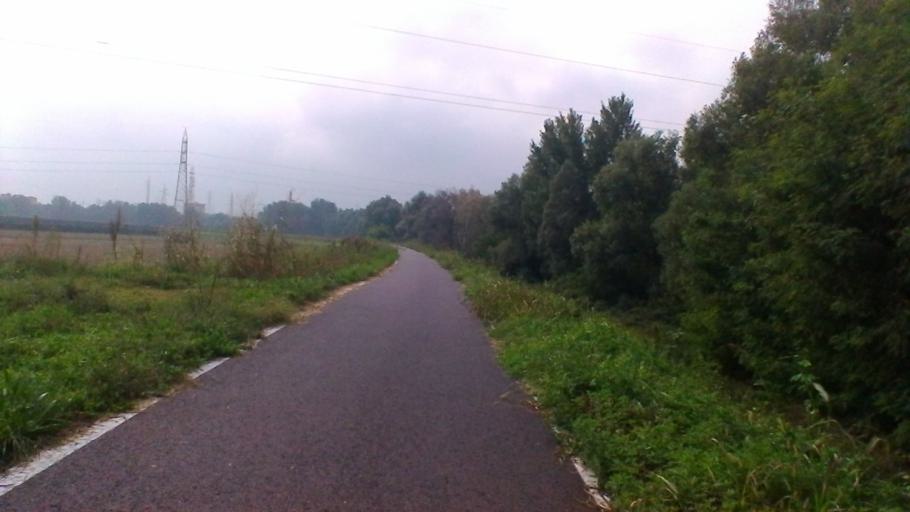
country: IT
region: Veneto
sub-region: Provincia di Verona
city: San Giovanni Lupatoto
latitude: 45.4005
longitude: 11.0328
